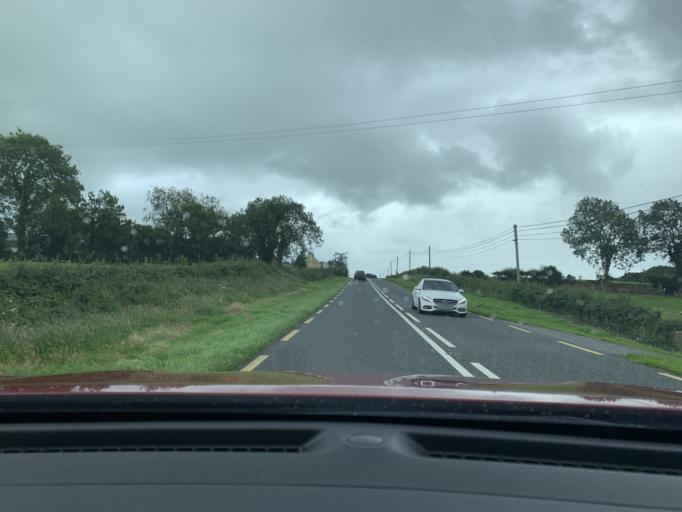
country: IE
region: Ulster
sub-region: County Donegal
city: Raphoe
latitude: 54.7990
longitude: -7.5716
